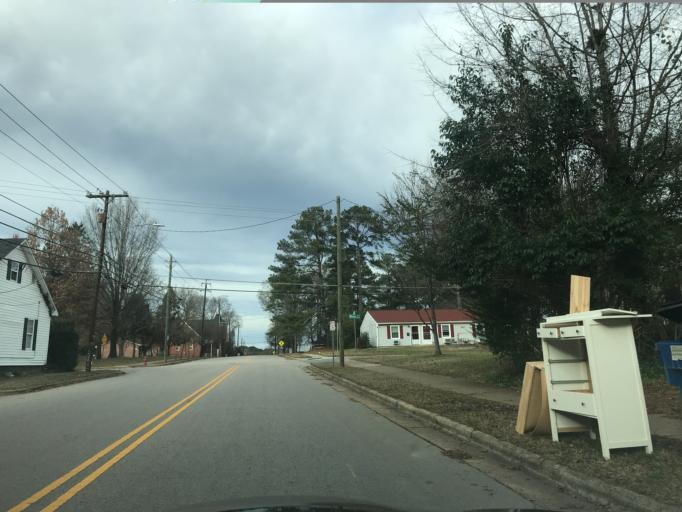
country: US
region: North Carolina
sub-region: Wake County
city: West Raleigh
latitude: 35.7914
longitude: -78.6937
